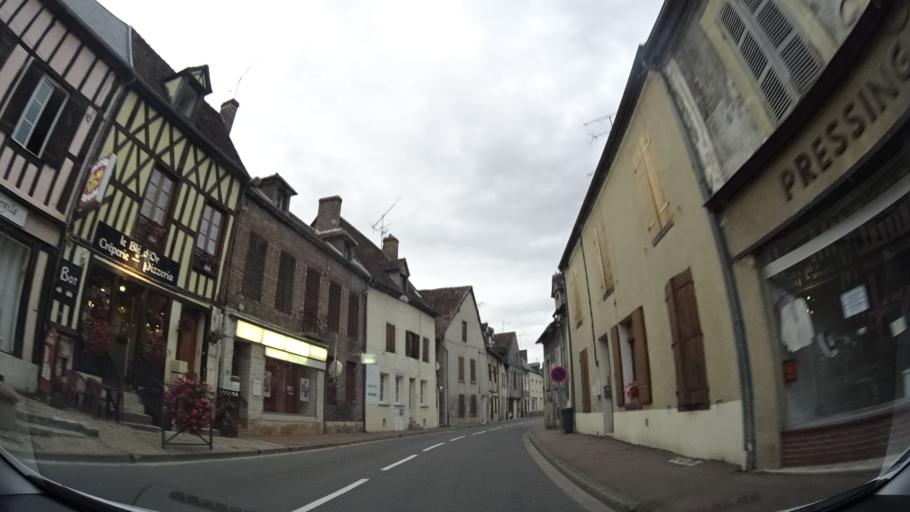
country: FR
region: Centre
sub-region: Departement du Loiret
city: Trigueres
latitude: 47.9329
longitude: 2.9280
